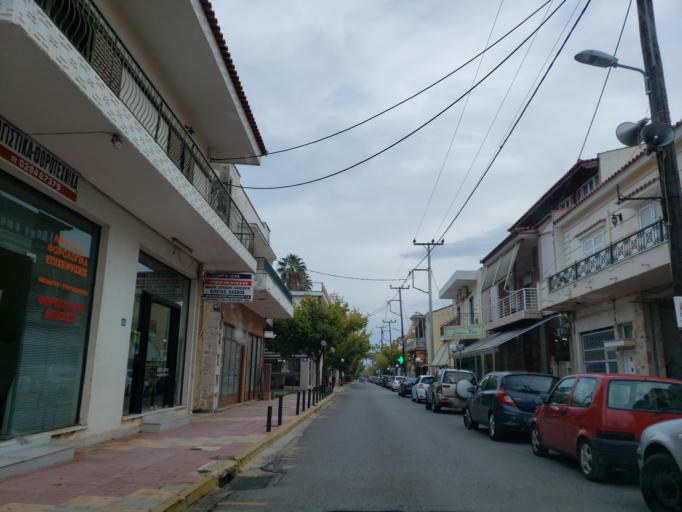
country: GR
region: Attica
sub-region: Nomarchia Anatolikis Attikis
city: Marathonas
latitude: 38.1557
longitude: 23.9604
